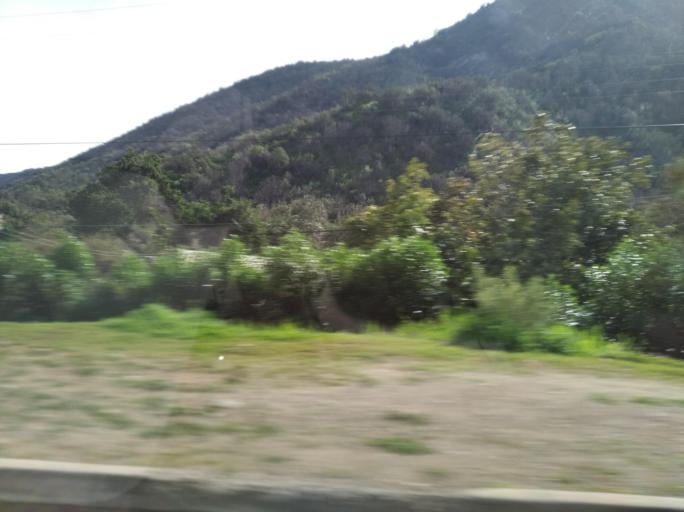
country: CL
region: Valparaiso
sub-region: Provincia de Marga Marga
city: Limache
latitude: -33.0637
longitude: -71.0706
